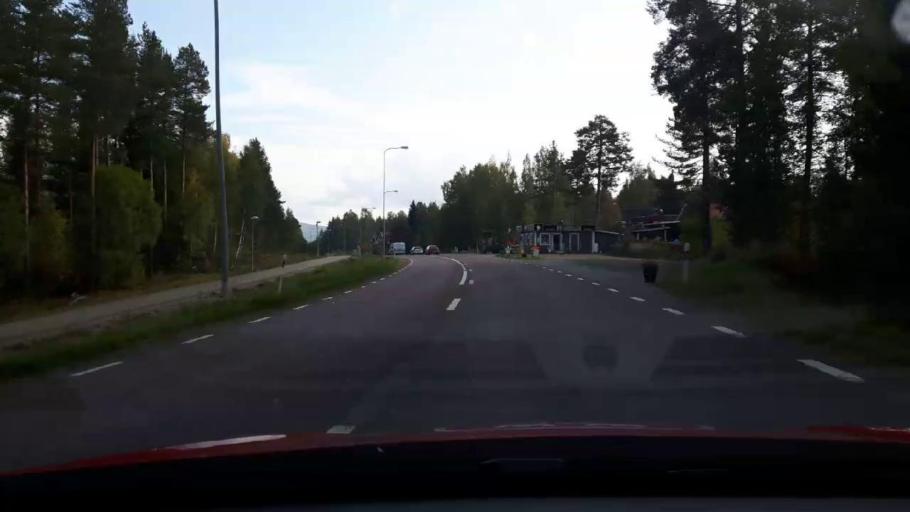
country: SE
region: Gaevleborg
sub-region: Bollnas Kommun
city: Kilafors
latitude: 61.2168
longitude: 16.5893
